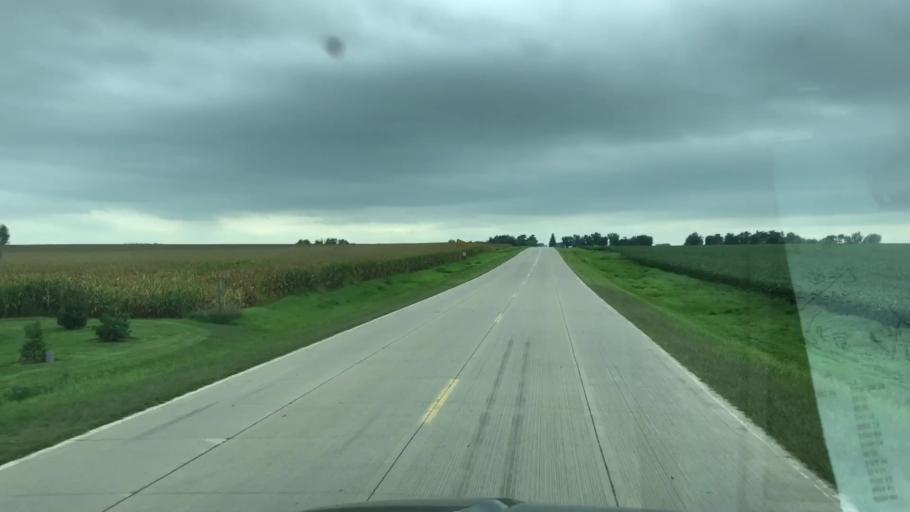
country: US
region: Iowa
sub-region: Sioux County
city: Alton
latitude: 43.1194
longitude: -95.9789
